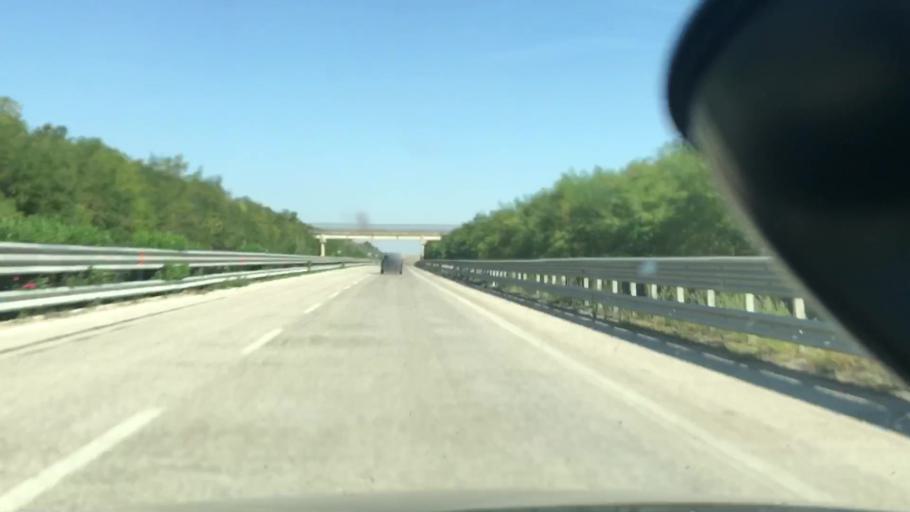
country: IT
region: Apulia
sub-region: Provincia di Foggia
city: Ordona
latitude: 41.2902
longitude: 15.5540
